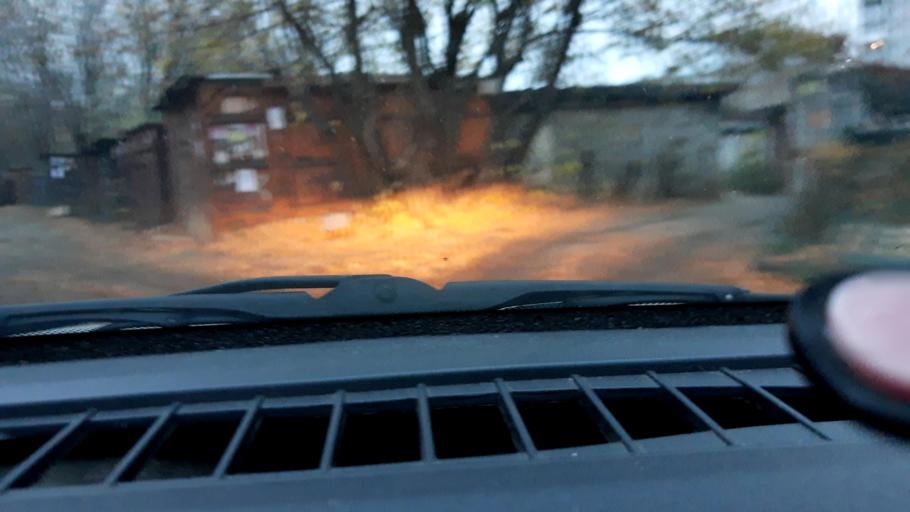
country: RU
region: Nizjnij Novgorod
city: Nizhniy Novgorod
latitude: 56.3302
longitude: 43.9227
